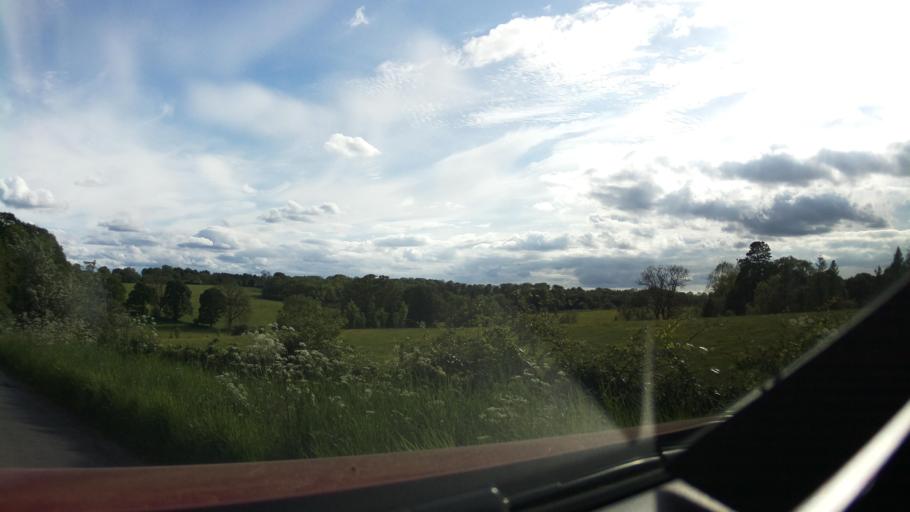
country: GB
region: England
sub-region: Gloucestershire
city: Stow on the Wold
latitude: 51.9400
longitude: -1.7939
